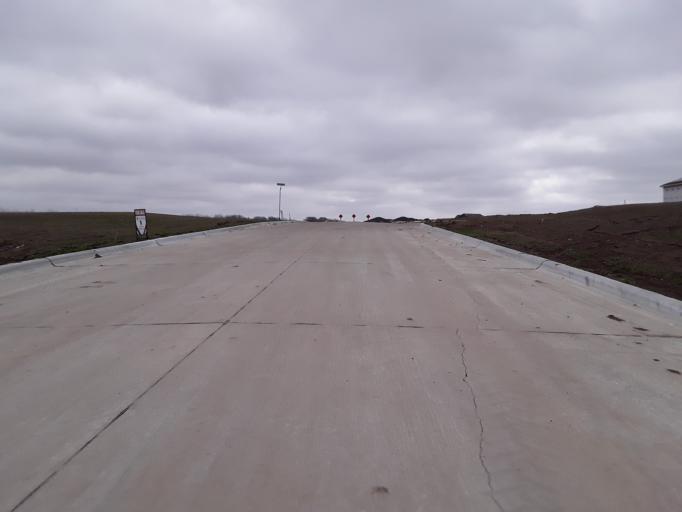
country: US
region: Nebraska
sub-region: Lancaster County
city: Lincoln
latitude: 40.8484
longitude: -96.5972
